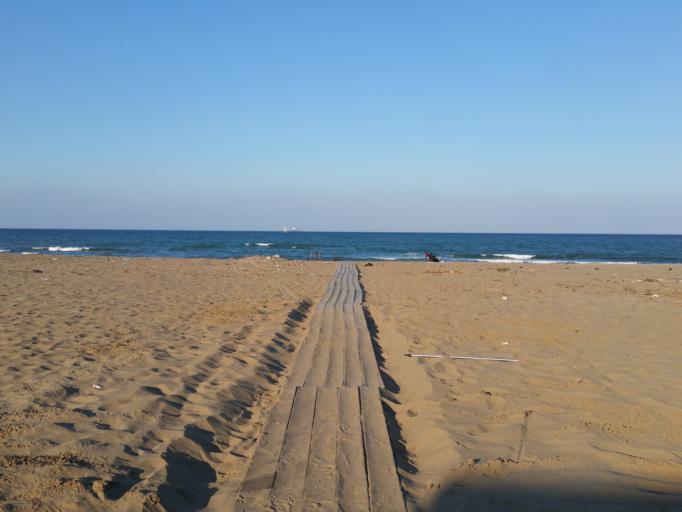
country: IT
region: Sicily
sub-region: Catania
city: Catania
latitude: 37.4475
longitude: 15.0861
